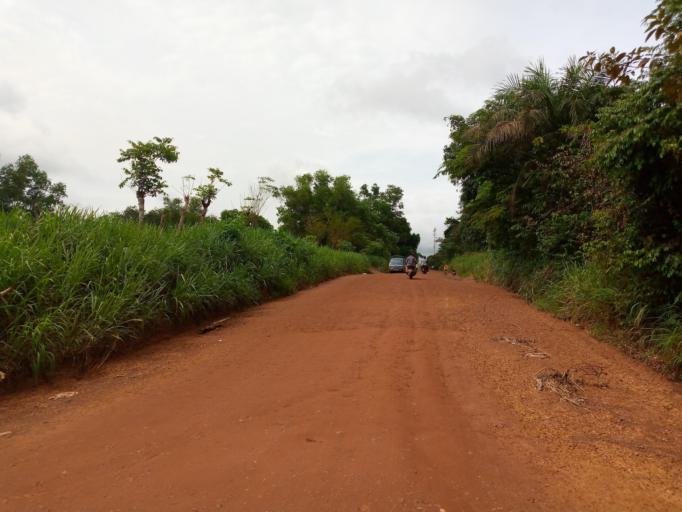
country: SL
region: Southern Province
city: Mogbwemo
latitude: 7.7708
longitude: -12.2963
